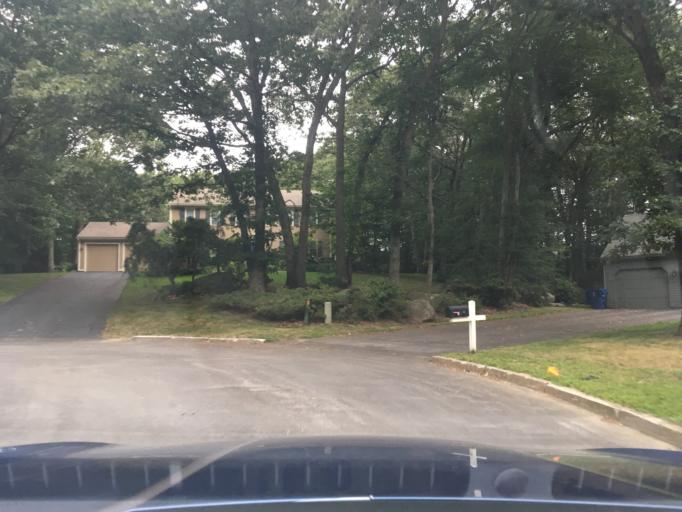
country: US
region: Rhode Island
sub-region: Kent County
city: East Greenwich
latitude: 41.6316
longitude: -71.5052
